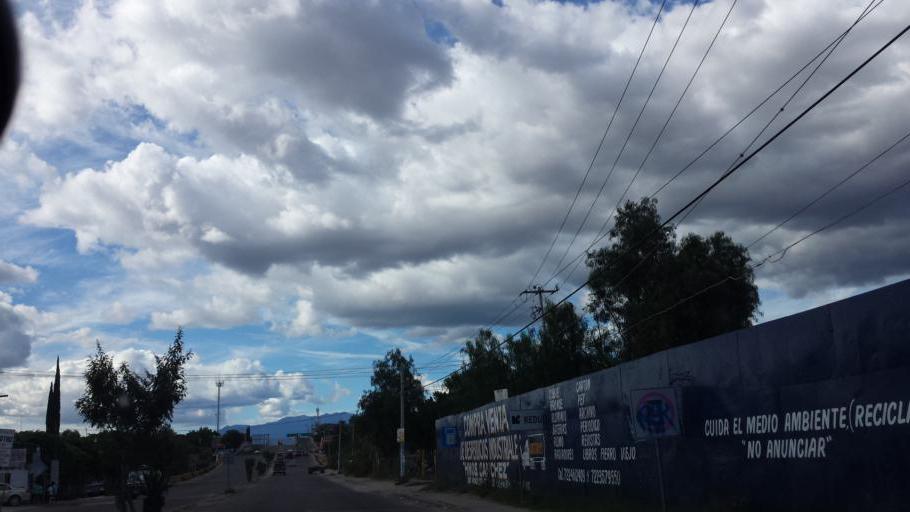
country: MX
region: Oaxaca
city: Tlacolula de Matamoros
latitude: 16.9549
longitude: -96.4705
